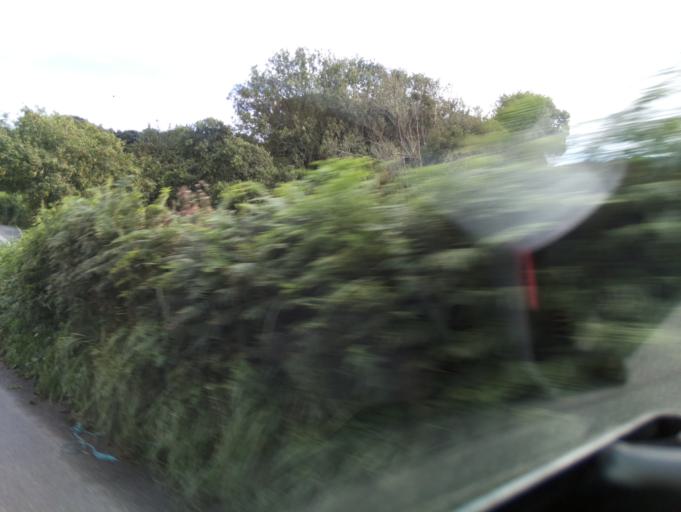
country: GB
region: England
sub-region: Devon
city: Modbury
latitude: 50.3432
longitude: -3.8794
